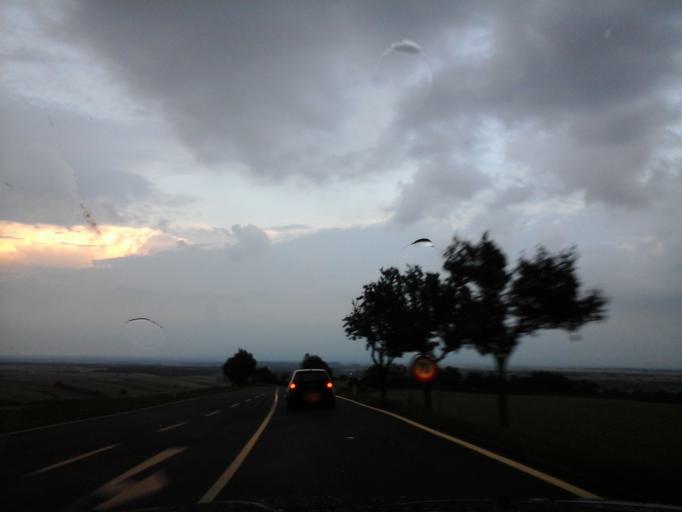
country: AT
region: Lower Austria
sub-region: Politischer Bezirk Ganserndorf
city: Zistersdorf
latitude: 48.5594
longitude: 16.7281
